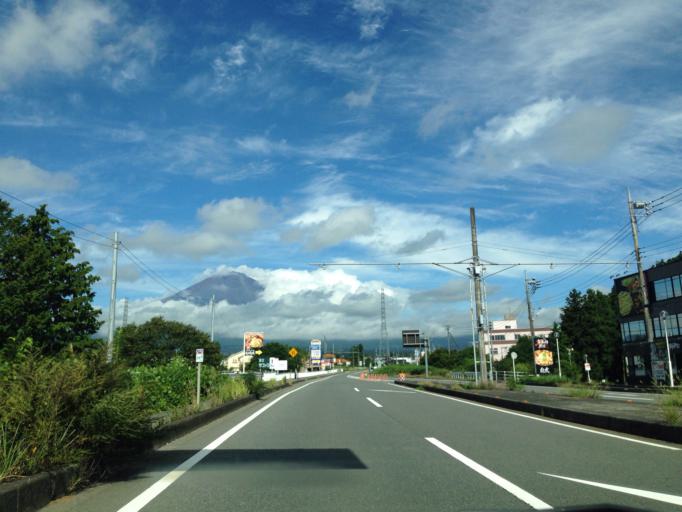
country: JP
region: Shizuoka
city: Gotemba
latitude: 35.3134
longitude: 138.9258
